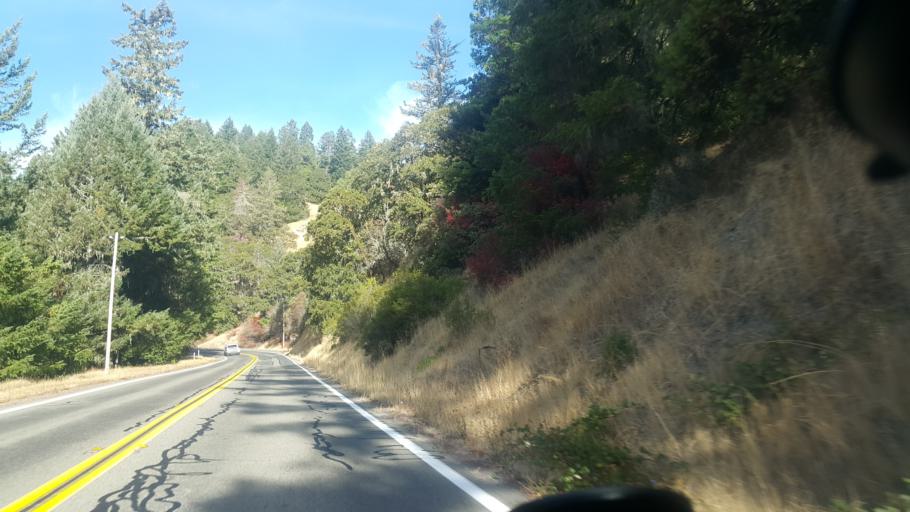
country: US
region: California
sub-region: Mendocino County
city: Brooktrails
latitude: 39.3882
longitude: -123.4303
